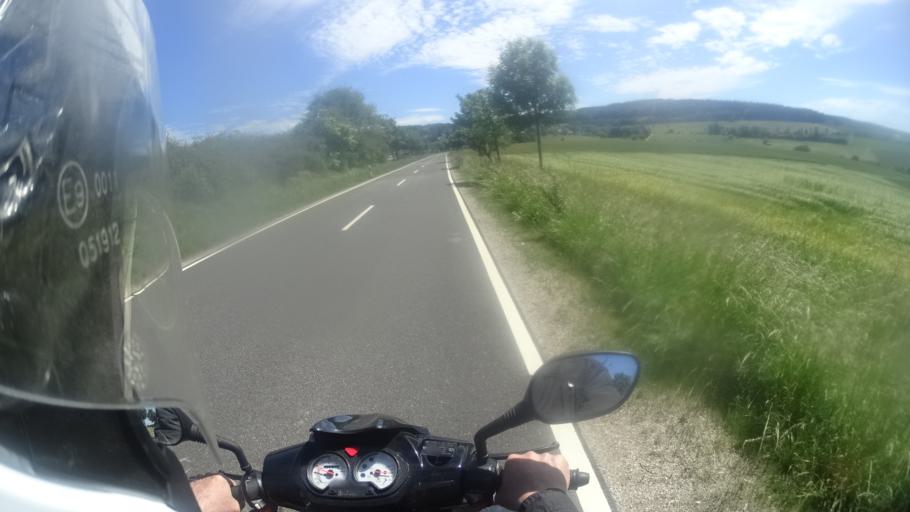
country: DE
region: Hesse
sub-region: Regierungsbezirk Darmstadt
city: Bad Schwalbach
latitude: 50.0894
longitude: 8.0411
